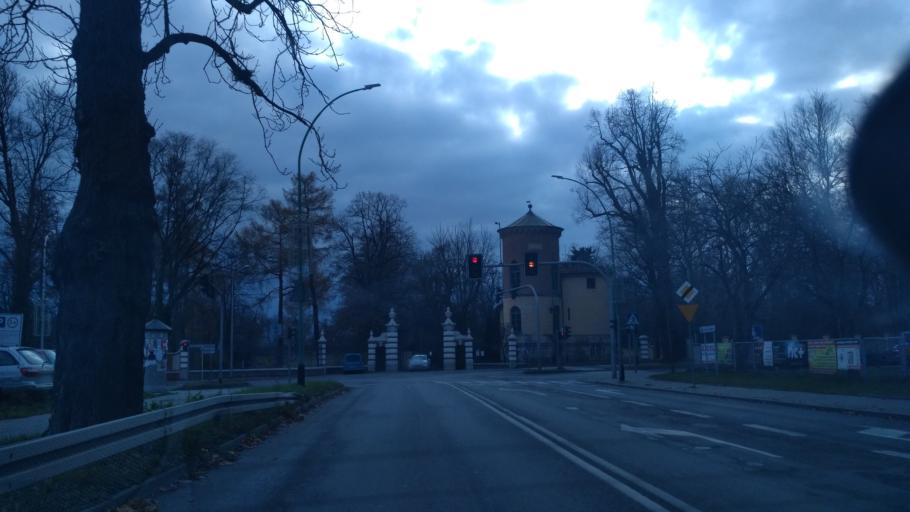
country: PL
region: Subcarpathian Voivodeship
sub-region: Powiat lancucki
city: Lancut
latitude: 50.0711
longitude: 22.2374
